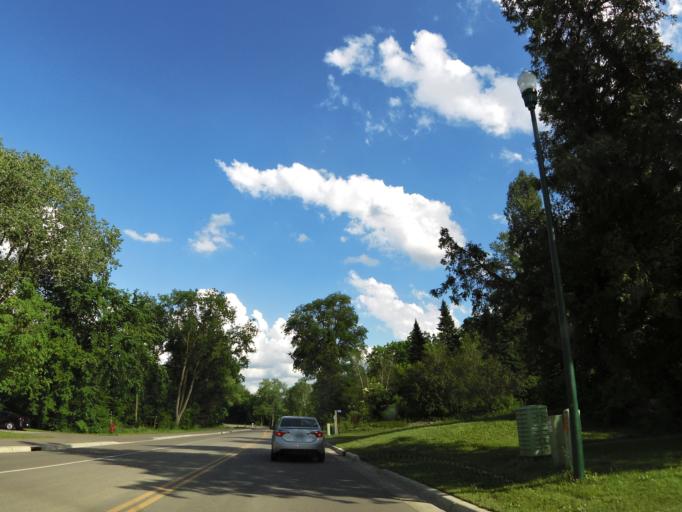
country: US
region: Minnesota
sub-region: Carver County
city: Chaska
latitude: 44.7930
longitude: -93.6111
